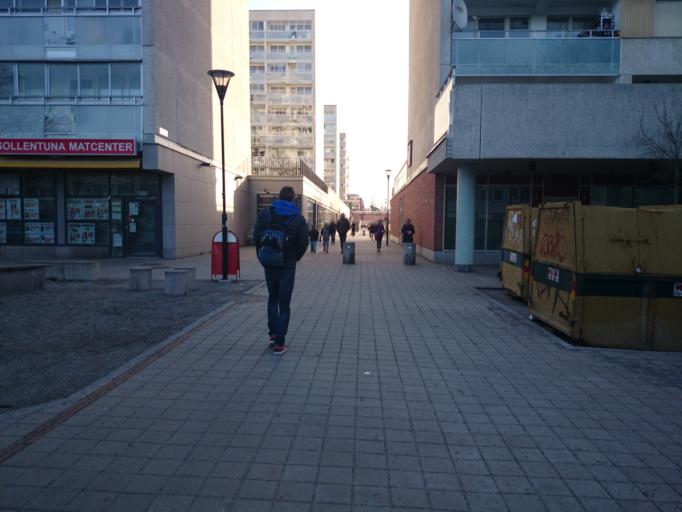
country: SE
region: Stockholm
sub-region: Sollentuna Kommun
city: Sollentuna
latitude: 59.4278
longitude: 17.9438
